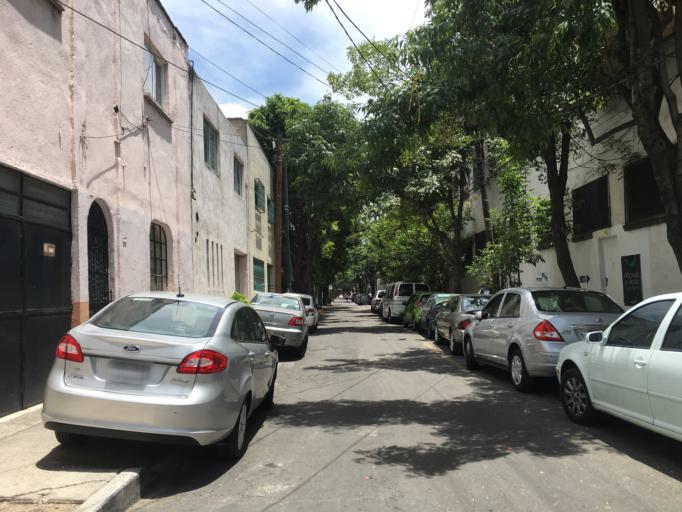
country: MX
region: Mexico City
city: Miguel Hidalgo
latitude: 19.4377
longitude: -99.1761
